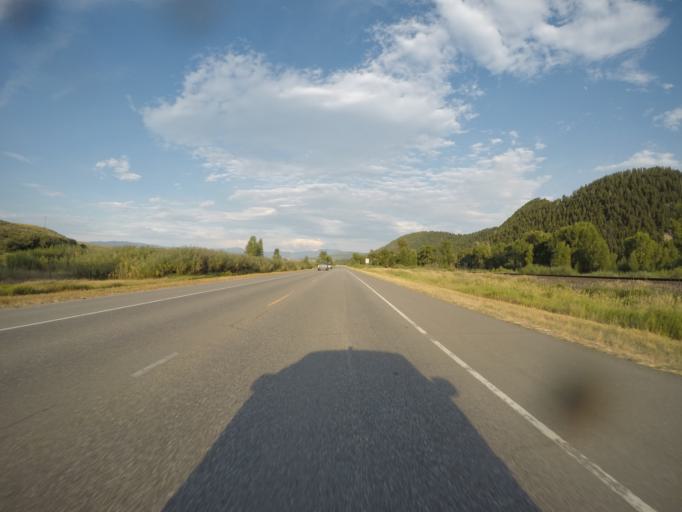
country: US
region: Colorado
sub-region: Routt County
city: Steamboat Springs
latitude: 40.4859
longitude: -106.9927
